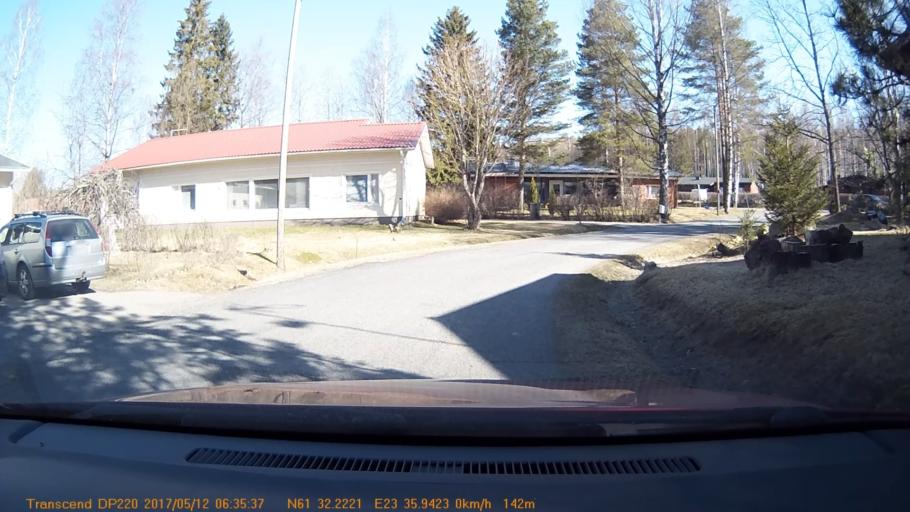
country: FI
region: Pirkanmaa
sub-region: Tampere
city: Yloejaervi
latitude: 61.5370
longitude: 23.5990
